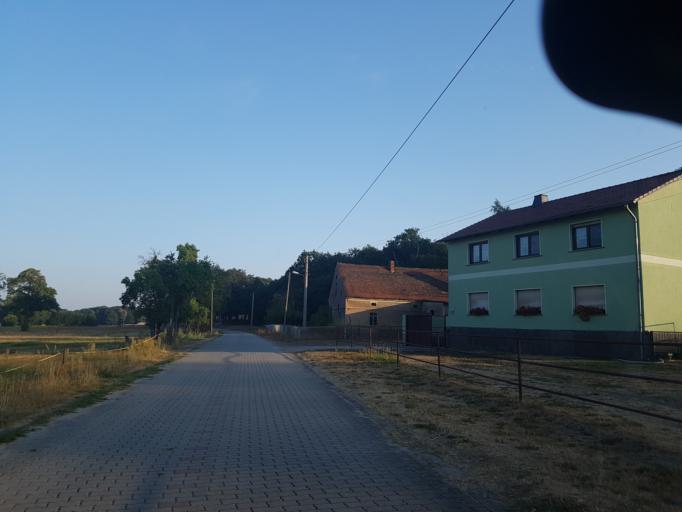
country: DE
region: Brandenburg
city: Falkenberg
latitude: 51.6435
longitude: 13.2938
